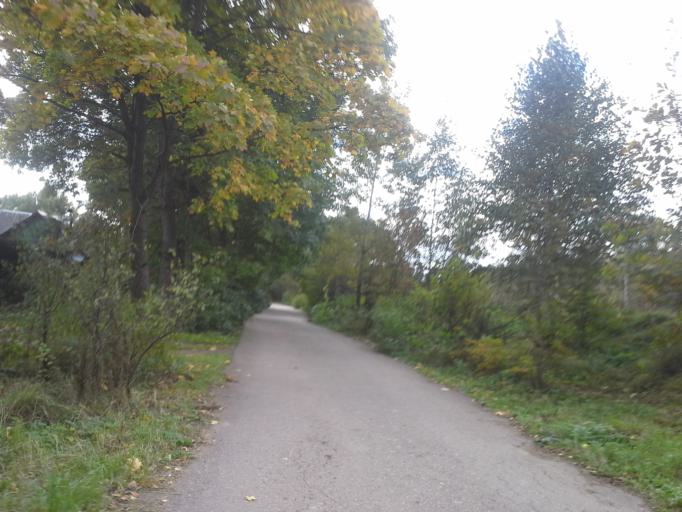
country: RU
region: Moskovskaya
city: Zhavoronki
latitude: 55.6363
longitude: 37.0689
